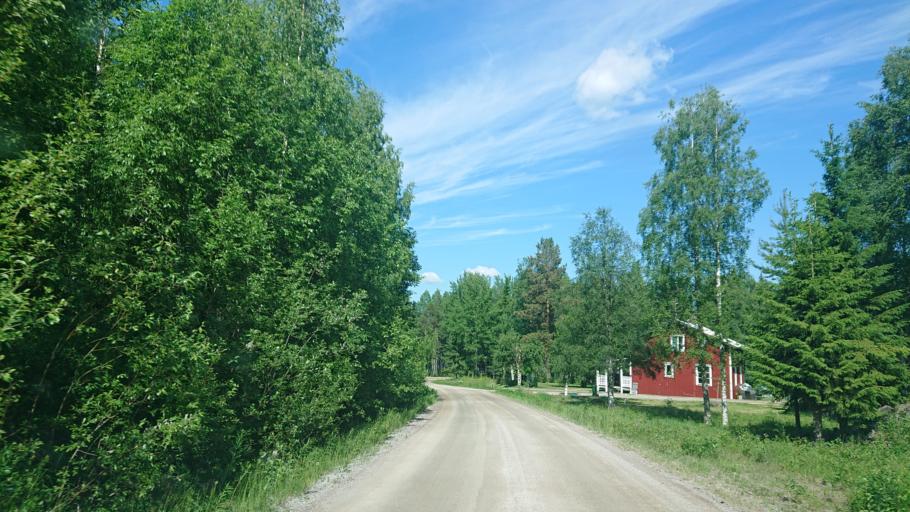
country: SE
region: Vaesternorrland
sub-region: Solleftea Kommun
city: Solleftea
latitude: 62.9690
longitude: 17.1598
